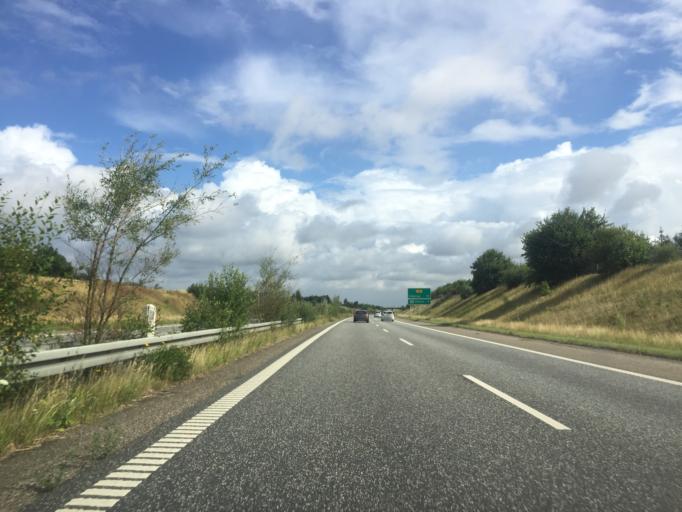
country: DK
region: South Denmark
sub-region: Faaborg-Midtfyn Kommune
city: Arslev
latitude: 55.3131
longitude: 10.4377
